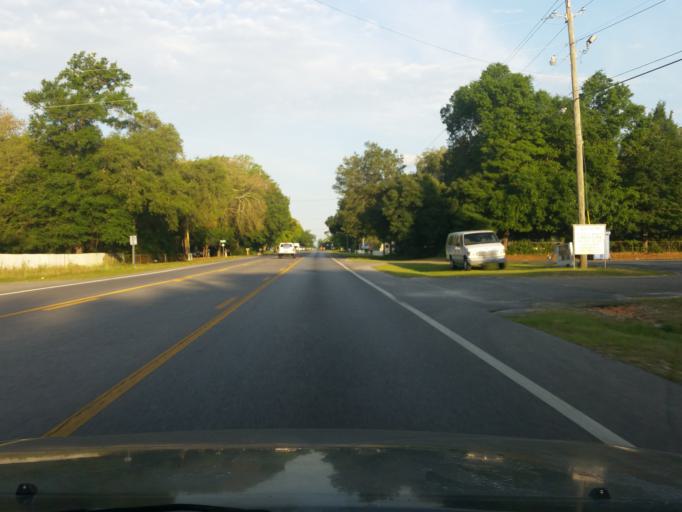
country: US
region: Florida
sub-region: Escambia County
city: Bellview
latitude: 30.4614
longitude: -87.3113
